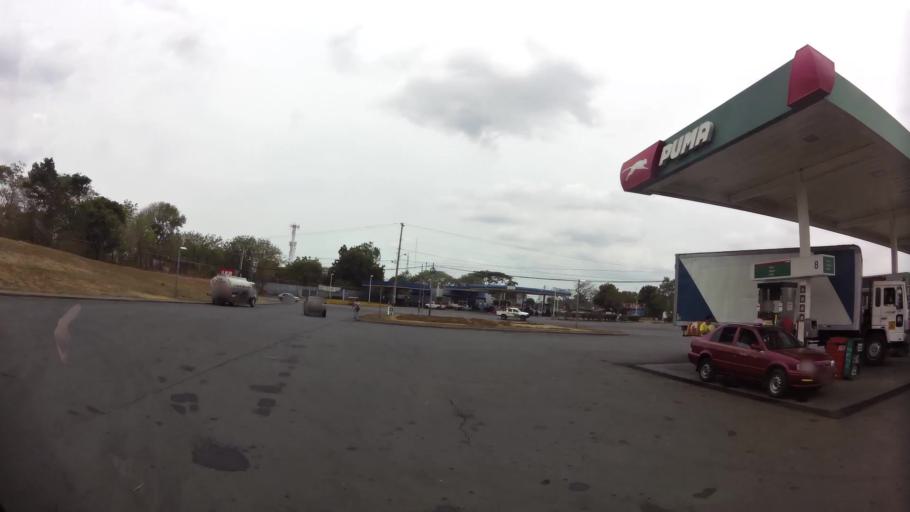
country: NI
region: Leon
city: Leon
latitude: 12.4583
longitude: -86.8676
